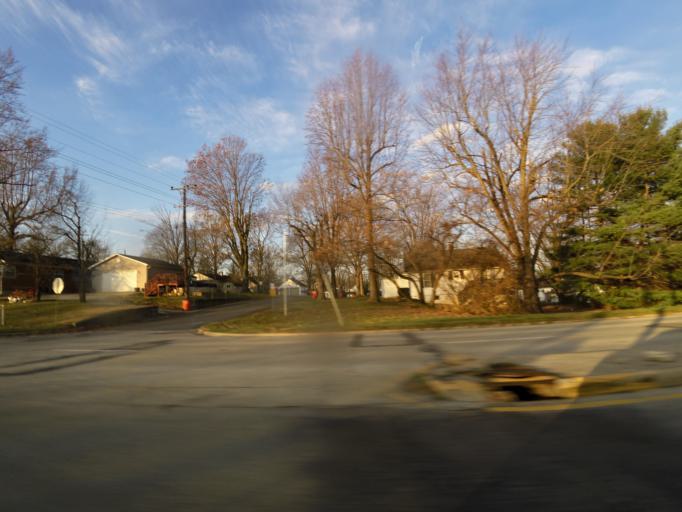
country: US
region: Illinois
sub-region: Fayette County
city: Vandalia
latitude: 38.9707
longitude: -89.0932
